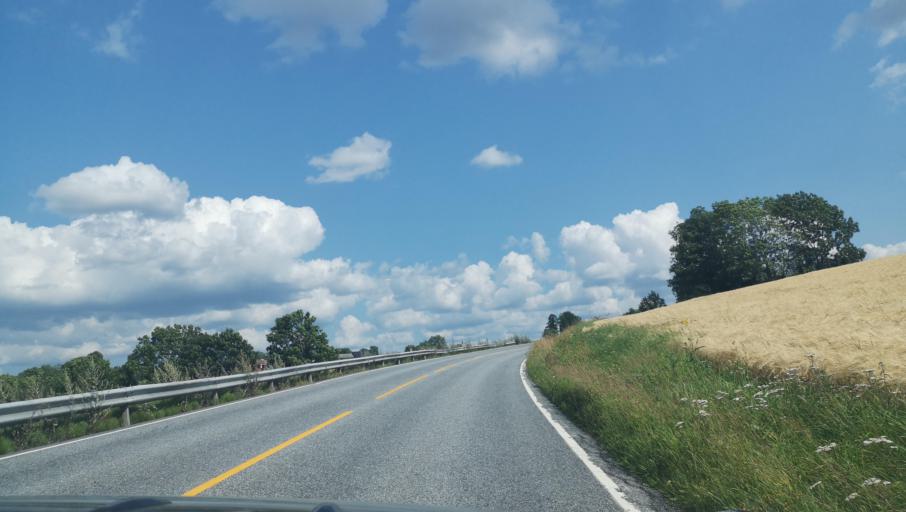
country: NO
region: Buskerud
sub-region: Ovre Eiker
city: Hokksund
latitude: 59.7286
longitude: 9.8380
